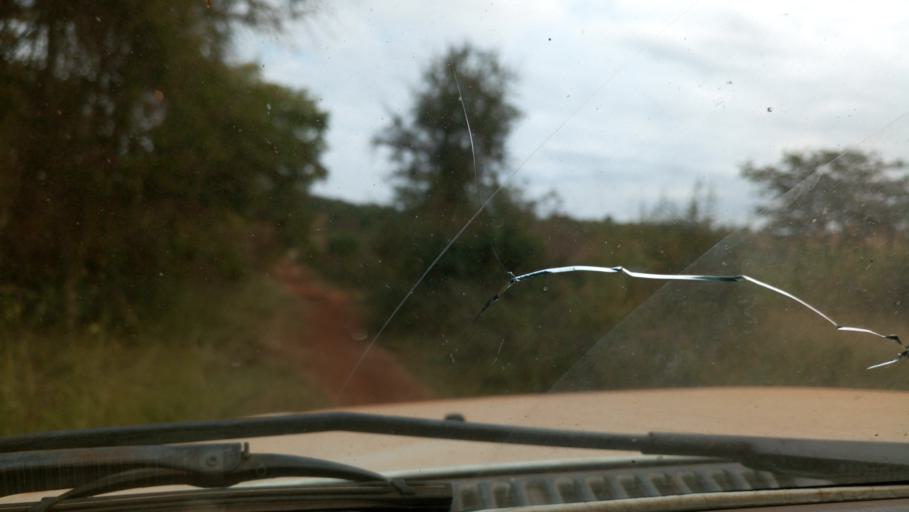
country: KE
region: Murang'a District
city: Karuri
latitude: -0.7585
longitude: 37.2122
